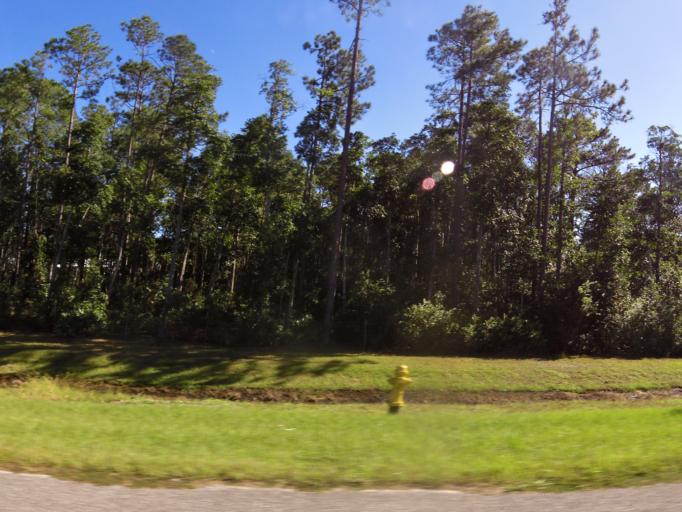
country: US
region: Florida
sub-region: Saint Johns County
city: Palm Valley
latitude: 30.1064
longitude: -81.4566
